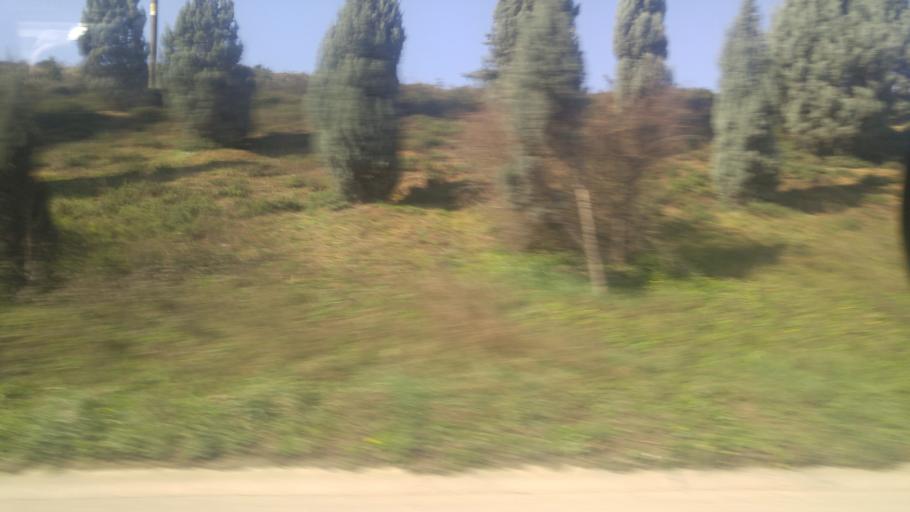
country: TR
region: Kocaeli
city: Balcik
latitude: 40.8486
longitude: 29.3748
